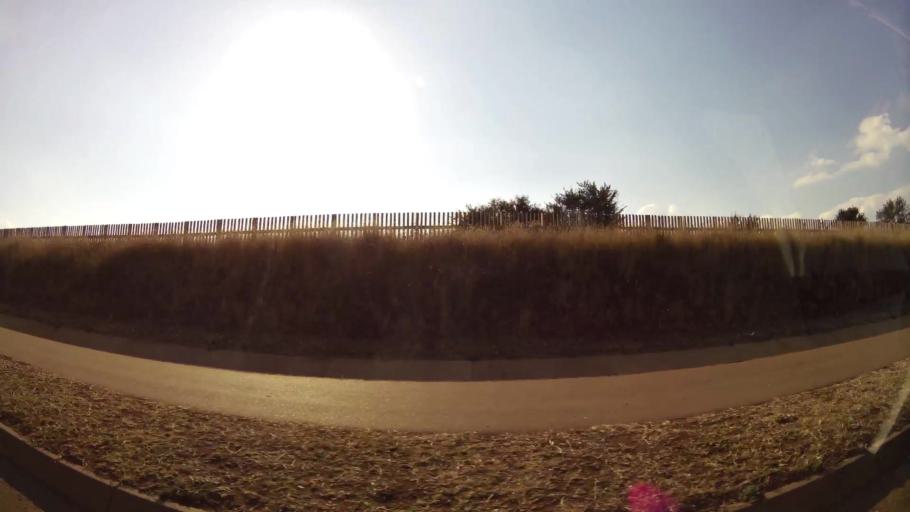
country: ZA
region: Gauteng
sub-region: City of Tshwane Metropolitan Municipality
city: Centurion
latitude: -25.9162
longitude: 28.2122
